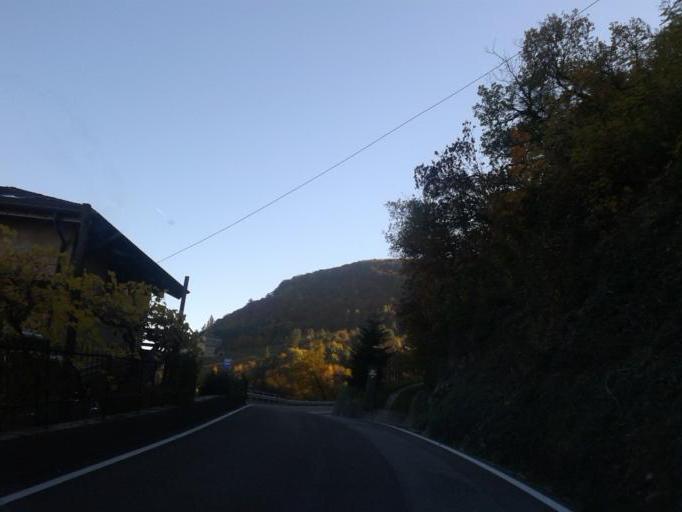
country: IT
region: Trentino-Alto Adige
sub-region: Provincia di Trento
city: Trento
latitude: 46.0754
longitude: 11.0982
